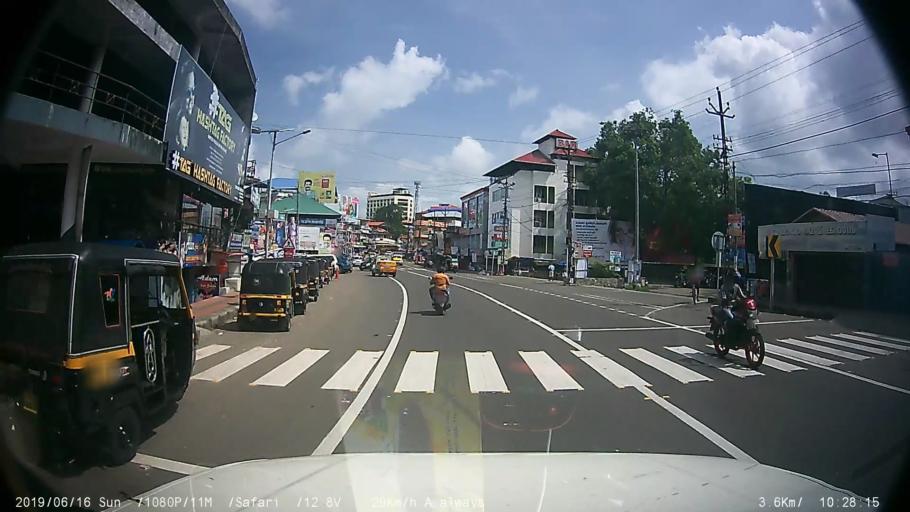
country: IN
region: Kerala
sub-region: Kottayam
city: Changanacheri
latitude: 9.4428
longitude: 76.5438
